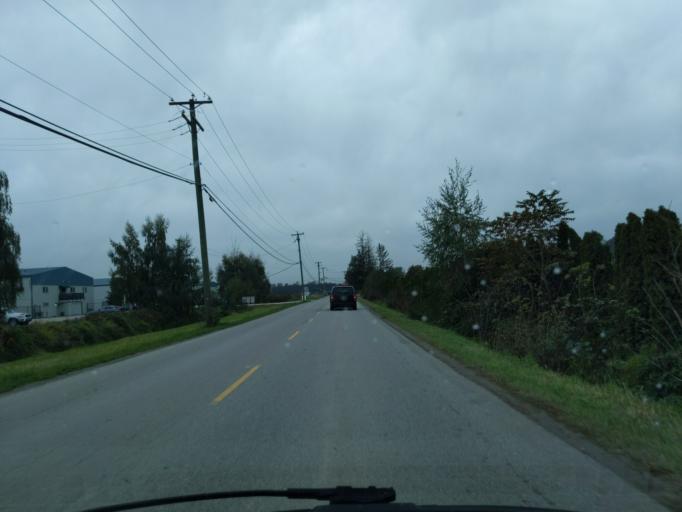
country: CA
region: British Columbia
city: Pitt Meadows
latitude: 49.2226
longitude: -122.7147
